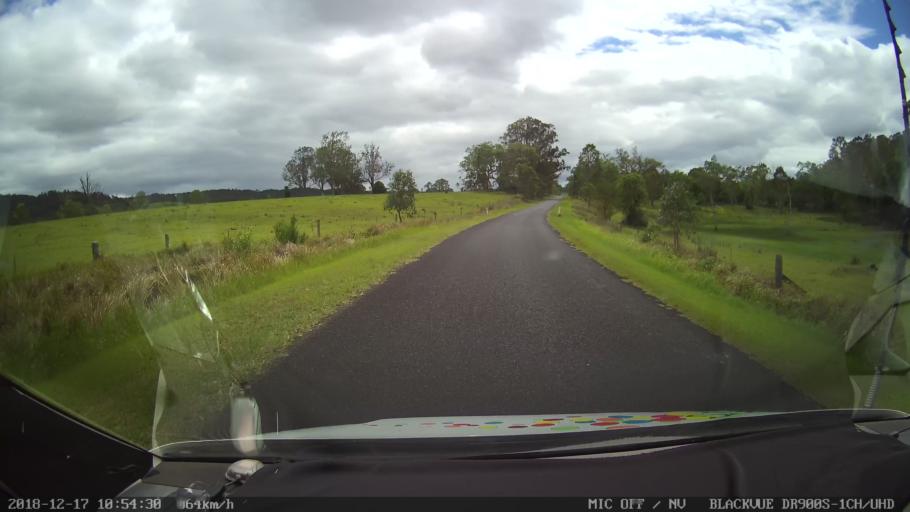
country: AU
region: New South Wales
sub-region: Tenterfield Municipality
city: Carrolls Creek
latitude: -28.8289
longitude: 152.5680
